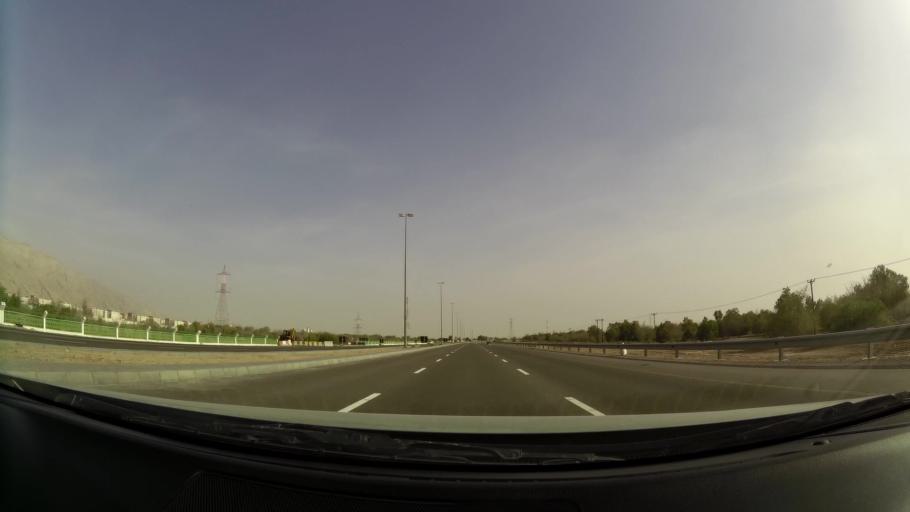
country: AE
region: Abu Dhabi
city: Al Ain
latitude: 24.0675
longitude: 55.7280
